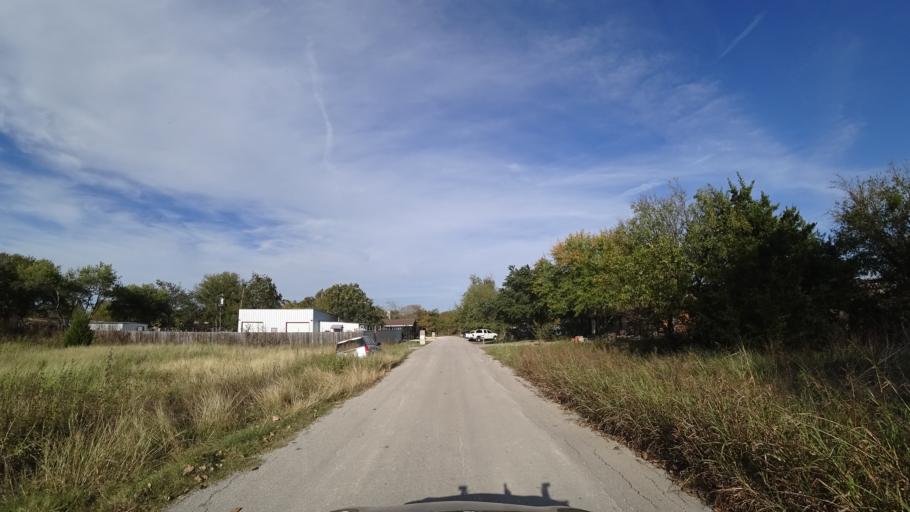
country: US
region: Texas
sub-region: Travis County
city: Wells Branch
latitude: 30.4753
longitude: -97.6845
